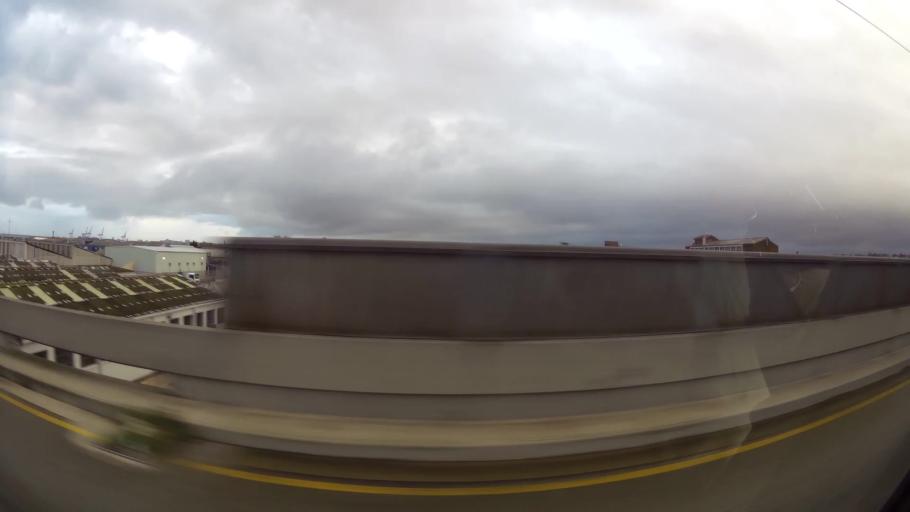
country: ZA
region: Eastern Cape
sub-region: Nelson Mandela Bay Metropolitan Municipality
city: Port Elizabeth
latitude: -33.9379
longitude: 25.6082
